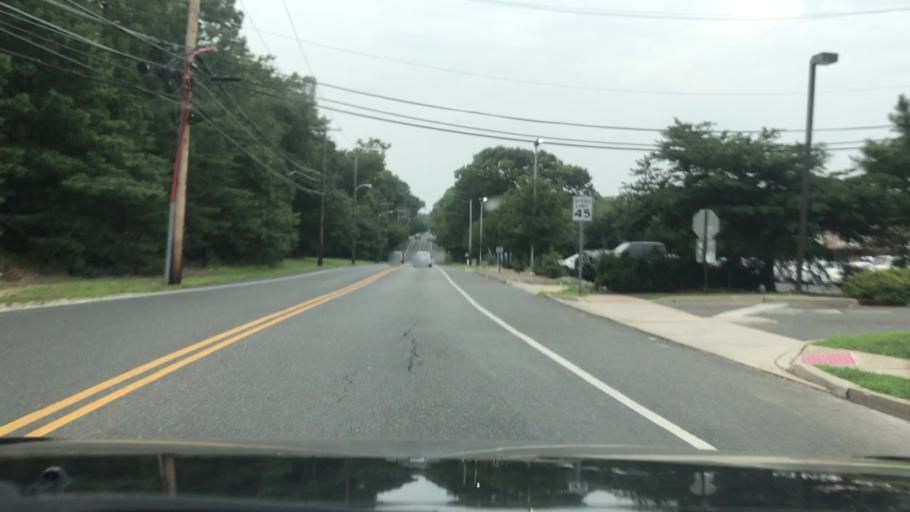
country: US
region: New Jersey
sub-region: Ocean County
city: Lakewood
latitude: 40.1274
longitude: -74.2554
